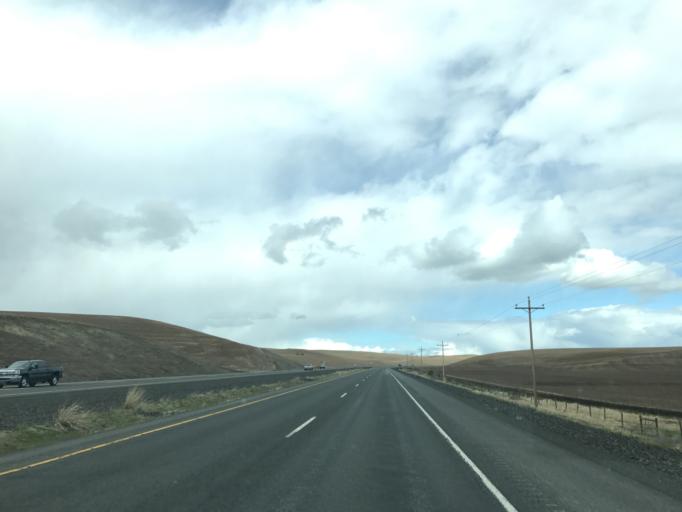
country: US
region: Idaho
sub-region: Nez Perce County
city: Lewiston
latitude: 46.5016
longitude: -116.9964
